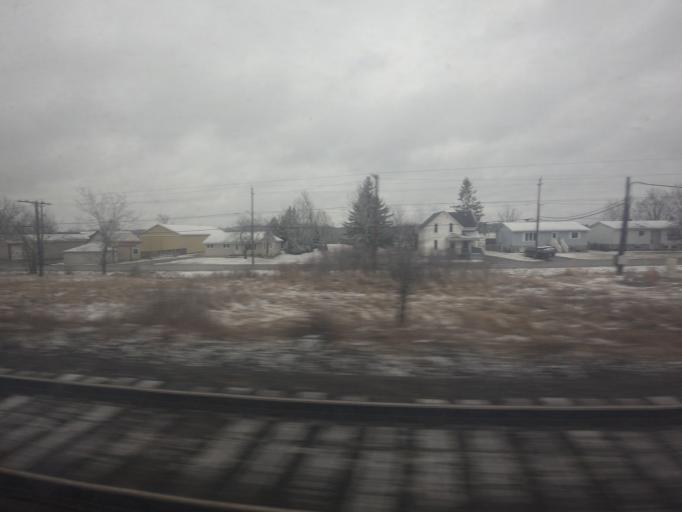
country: US
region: New York
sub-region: Jefferson County
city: Alexandria Bay
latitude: 44.4035
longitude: -76.0176
